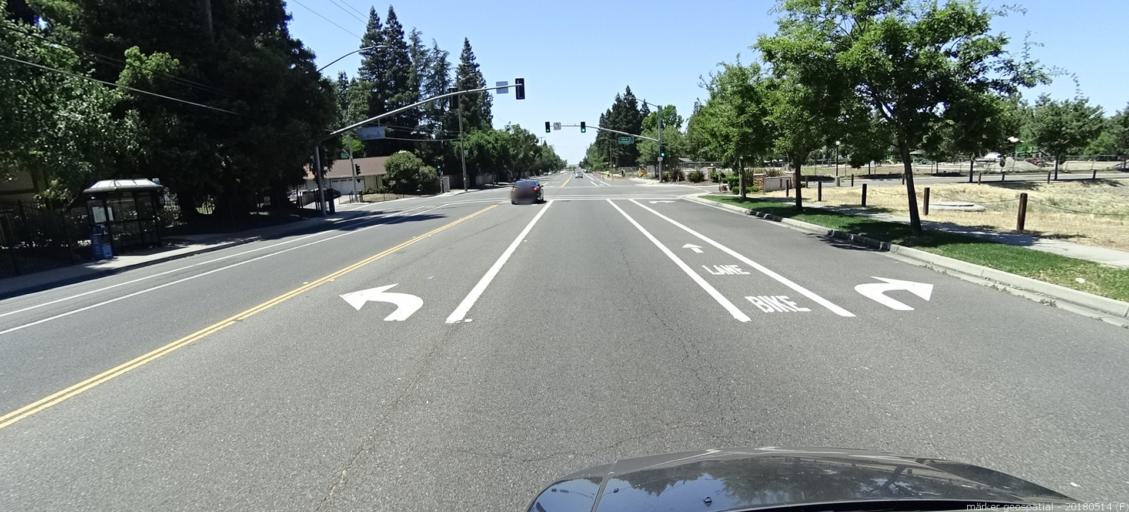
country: US
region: California
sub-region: Sacramento County
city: Sacramento
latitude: 38.6275
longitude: -121.5011
